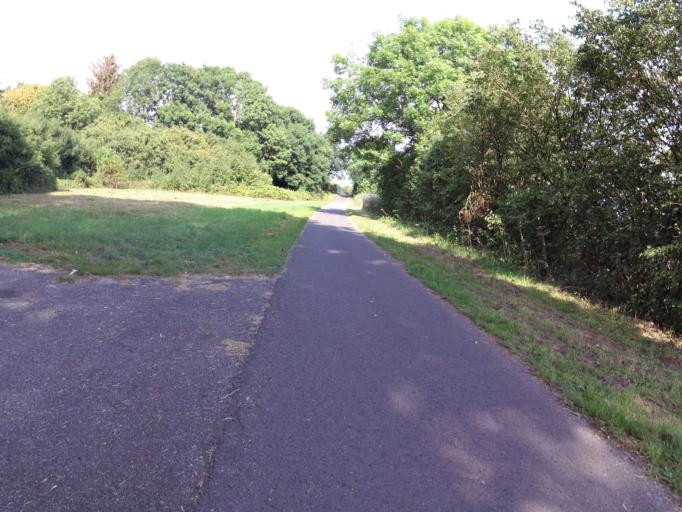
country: DE
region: North Rhine-Westphalia
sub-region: Regierungsbezirk Detmold
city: Petershagen
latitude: 52.3527
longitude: 8.9583
